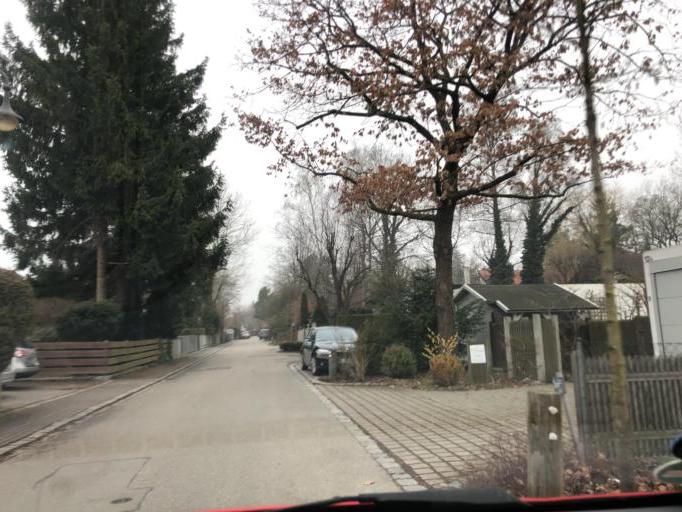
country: DE
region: Bavaria
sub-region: Upper Bavaria
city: Grobenzell
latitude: 48.2034
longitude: 11.3744
